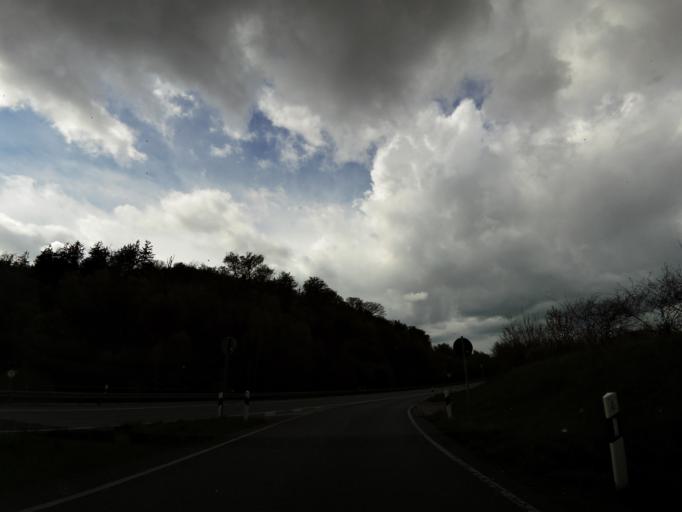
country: DE
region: Lower Saxony
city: Langelsheim
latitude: 51.9313
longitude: 10.3176
